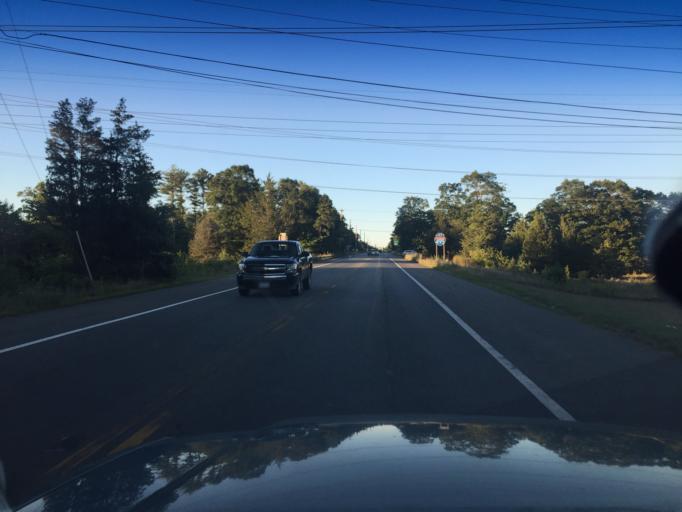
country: US
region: Massachusetts
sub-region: Plymouth County
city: West Wareham
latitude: 41.8033
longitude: -70.7719
